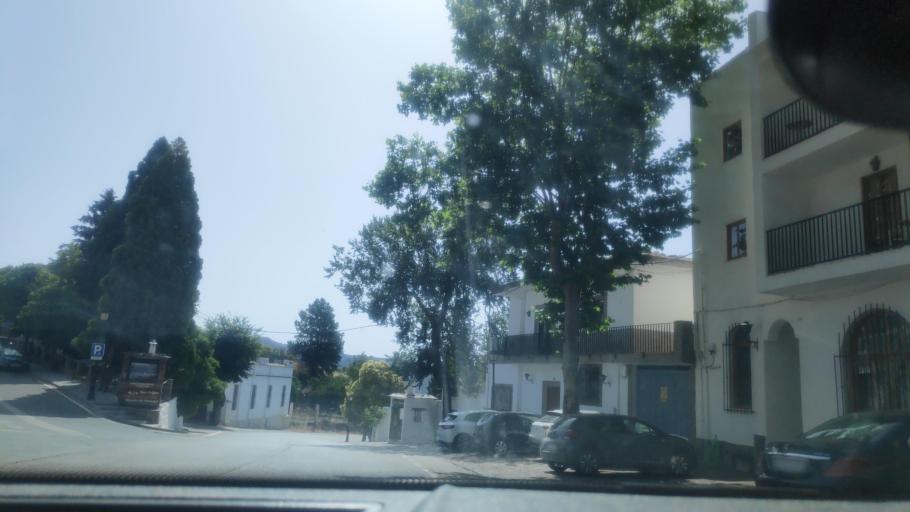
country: ES
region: Andalusia
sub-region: Provincia de Granada
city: Portugos
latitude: 36.9407
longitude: -3.3108
